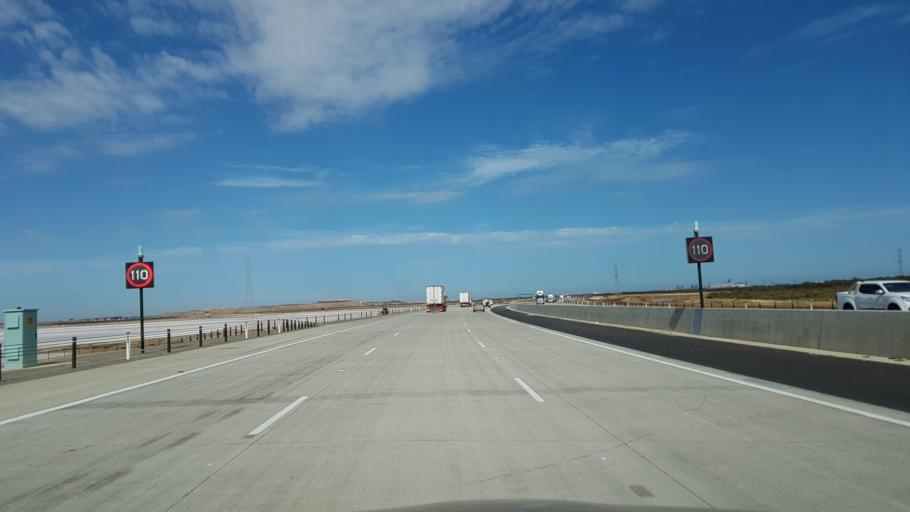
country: AU
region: South Australia
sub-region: Port Adelaide Enfield
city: Enfield
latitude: -34.8060
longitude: 138.5729
